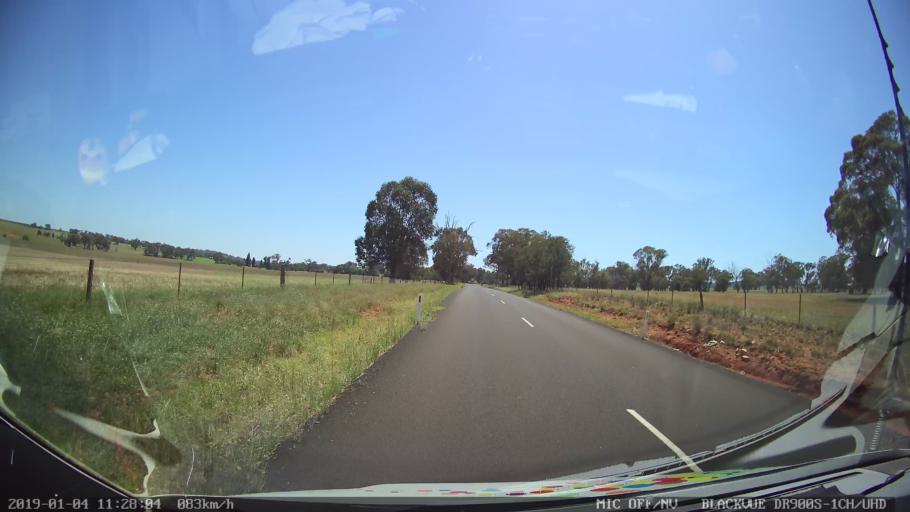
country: AU
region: New South Wales
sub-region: Cabonne
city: Molong
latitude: -33.1032
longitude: 148.7686
